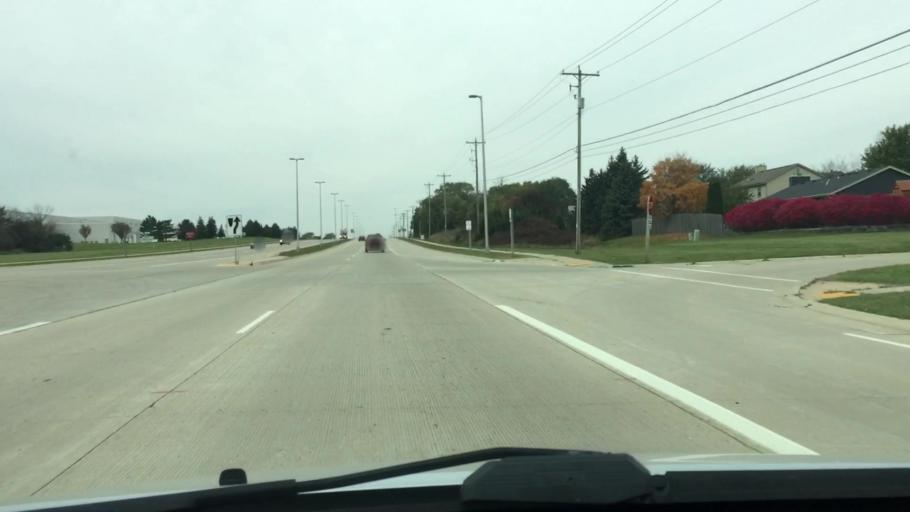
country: US
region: Wisconsin
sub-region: Milwaukee County
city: Franklin
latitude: 42.8728
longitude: -87.9708
